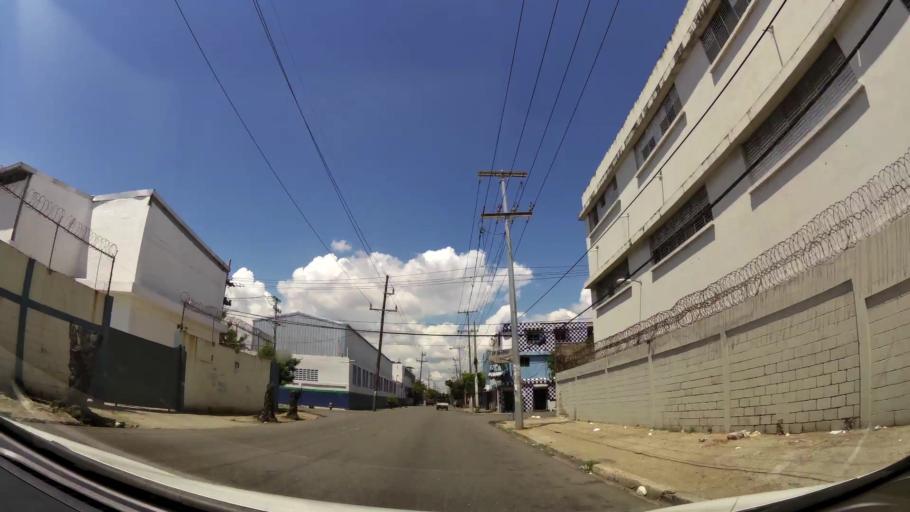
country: DO
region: Nacional
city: San Carlos
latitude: 18.4897
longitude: -69.8899
